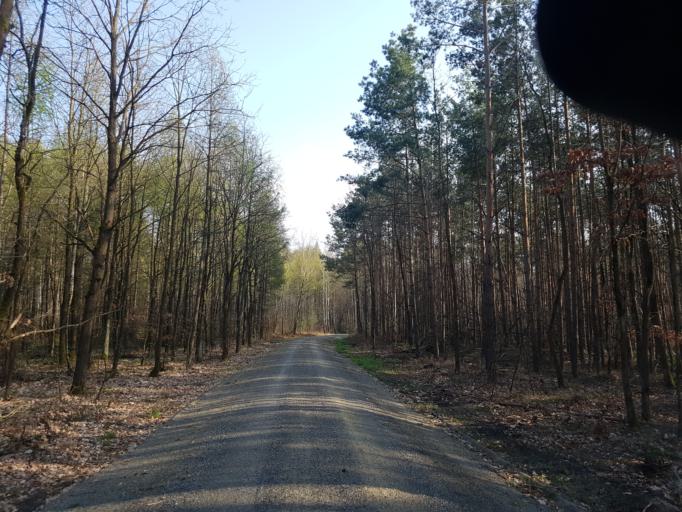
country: DE
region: Brandenburg
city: Schonborn
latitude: 51.6100
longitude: 13.5187
